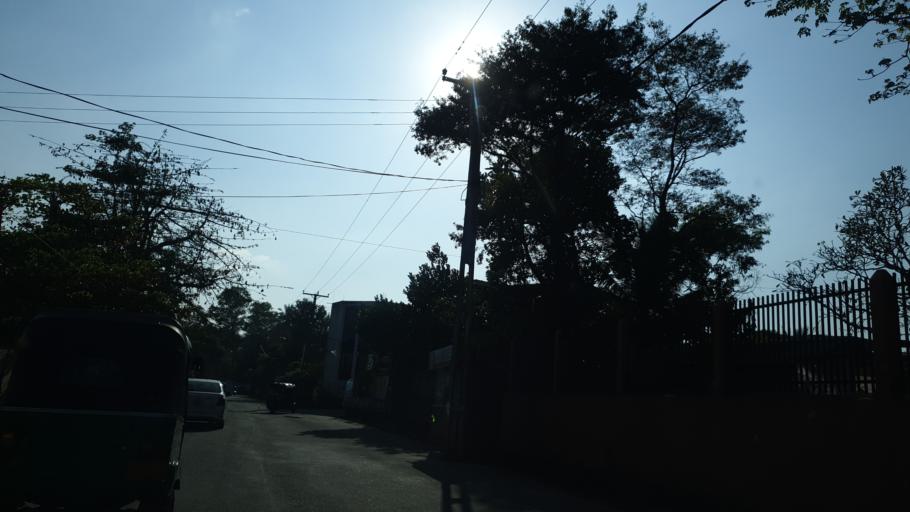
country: LK
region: Western
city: Sri Jayewardenepura Kotte
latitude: 6.8763
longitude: 79.9198
